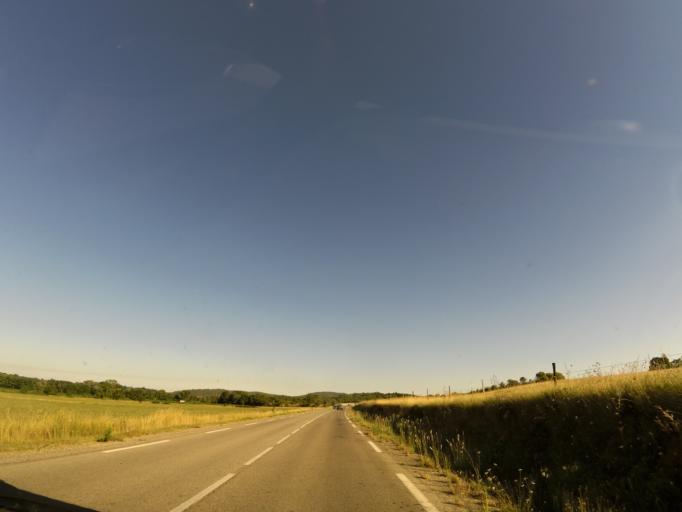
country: FR
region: Languedoc-Roussillon
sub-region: Departement du Gard
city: Quissac
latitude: 43.8866
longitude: 4.0050
